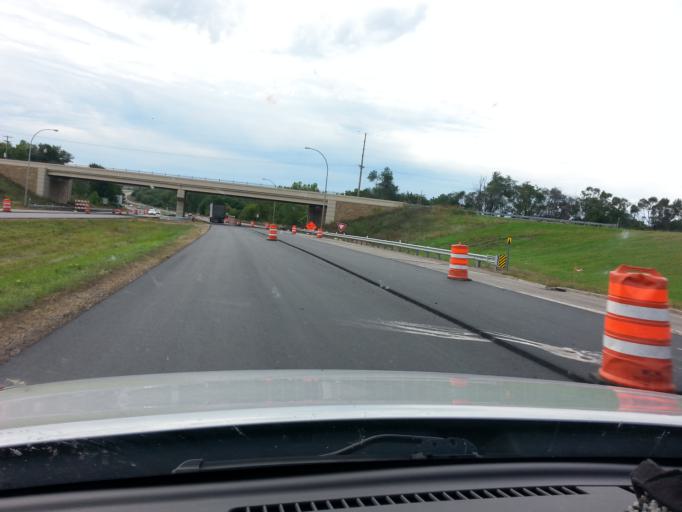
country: US
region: Minnesota
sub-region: Goodhue County
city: Cannon Falls
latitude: 44.5079
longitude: -92.9193
